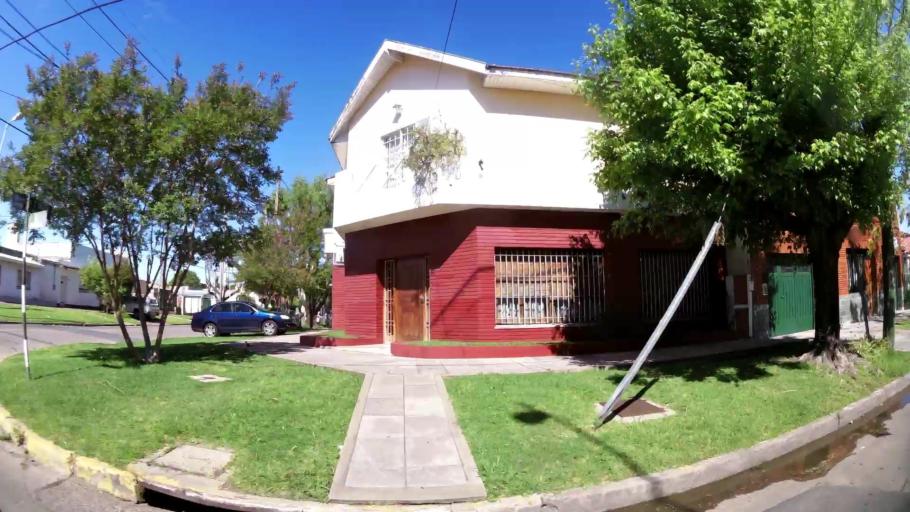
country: AR
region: Buenos Aires
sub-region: Partido de Lomas de Zamora
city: Lomas de Zamora
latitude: -34.7521
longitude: -58.4183
